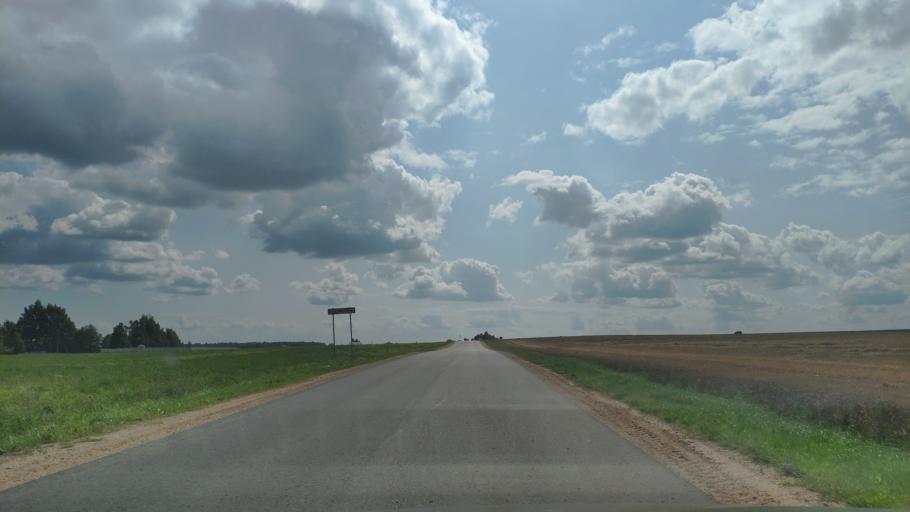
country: BY
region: Minsk
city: Khatsyezhyna
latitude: 53.8359
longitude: 27.3072
